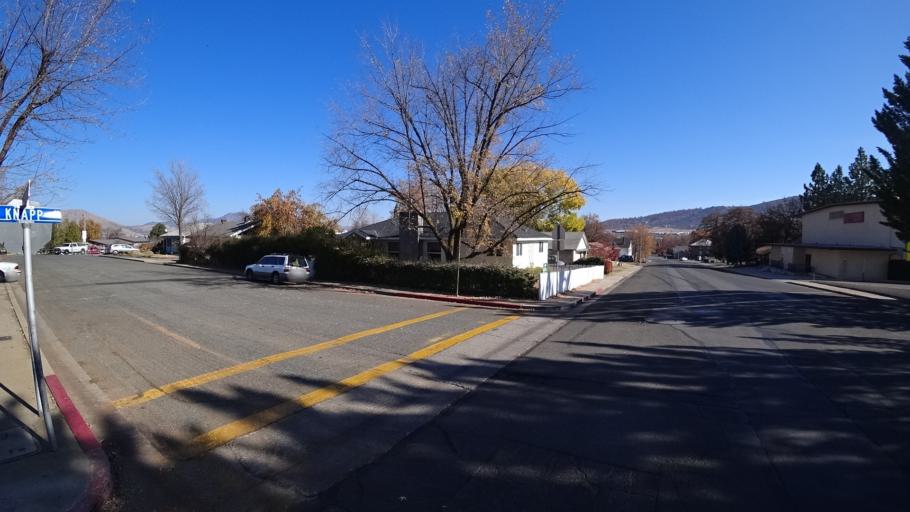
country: US
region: California
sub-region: Siskiyou County
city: Yreka
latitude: 41.7390
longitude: -122.6382
